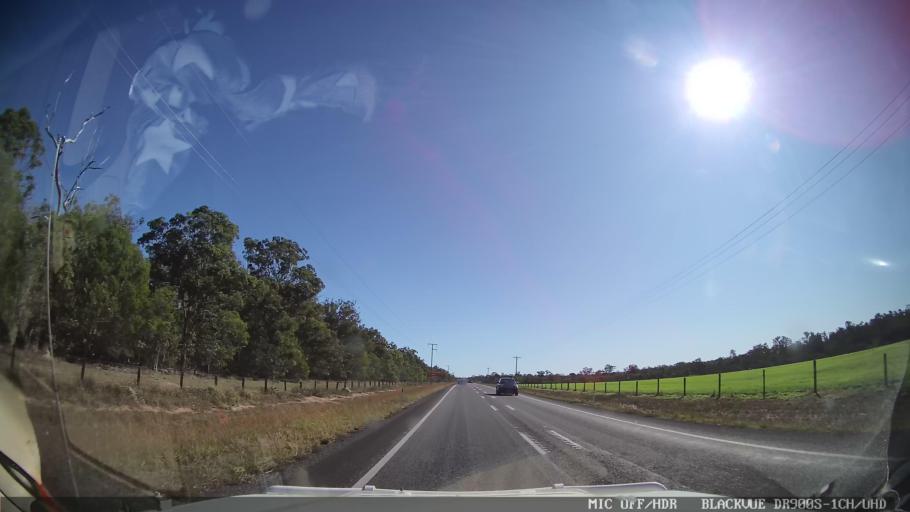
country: AU
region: Queensland
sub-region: Bundaberg
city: Childers
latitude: -25.2508
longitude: 152.3516
